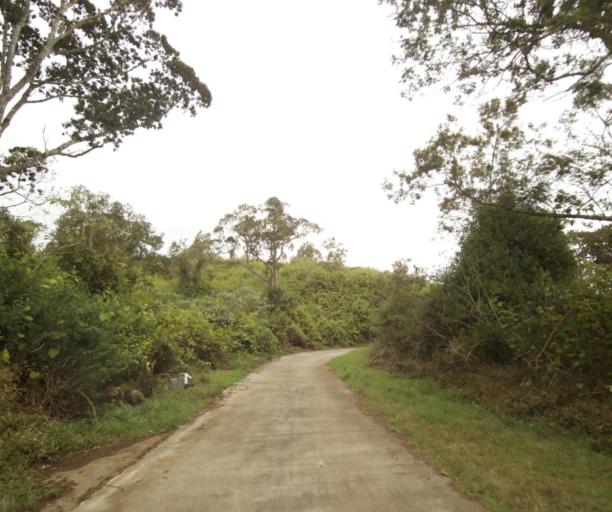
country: RE
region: Reunion
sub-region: Reunion
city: Saint-Paul
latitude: -21.0158
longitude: 55.3554
